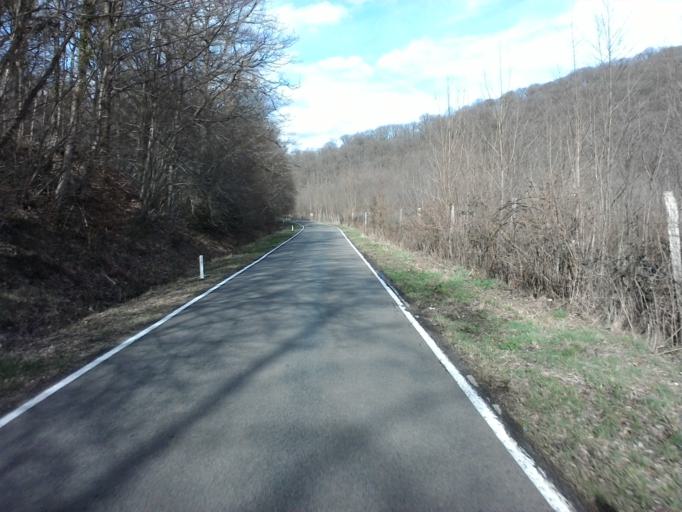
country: BE
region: Wallonia
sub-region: Province du Luxembourg
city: Daverdisse
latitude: 50.0399
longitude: 5.1374
